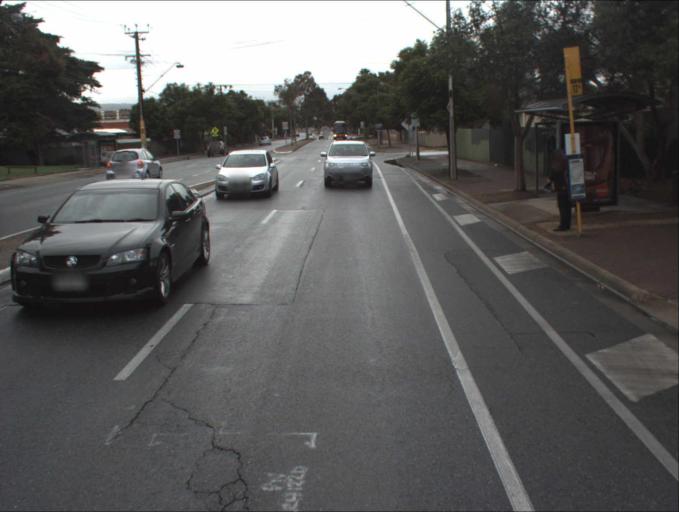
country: AU
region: South Australia
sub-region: Norwood Payneham St Peters
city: Marden
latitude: -34.8883
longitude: 138.6395
